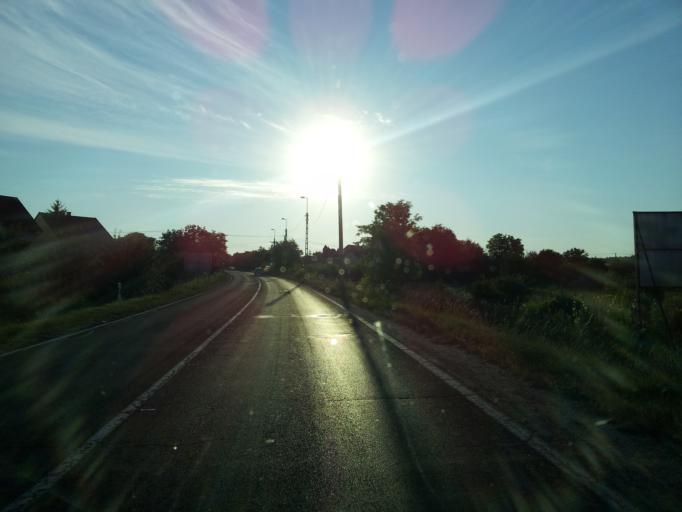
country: HU
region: Fejer
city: Bicske
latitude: 47.5012
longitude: 18.6269
